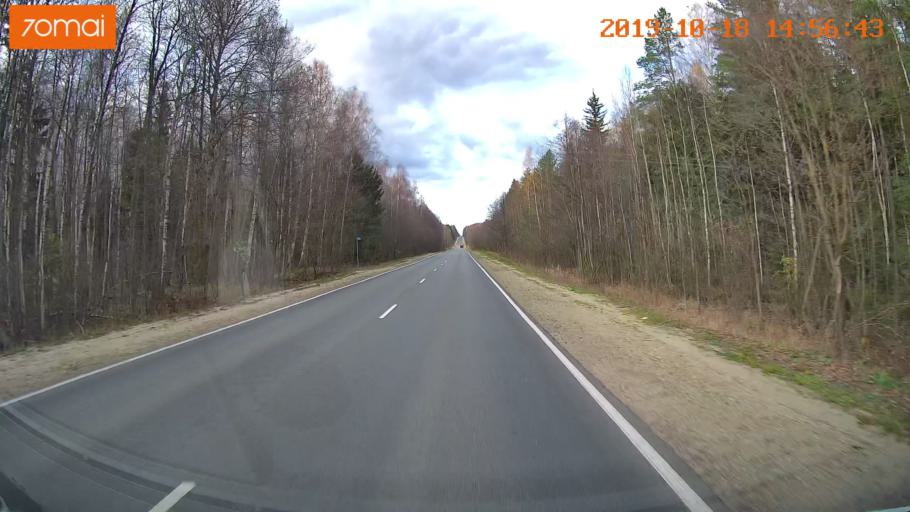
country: RU
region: Vladimir
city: Kurlovo
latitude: 55.4688
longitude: 40.5858
